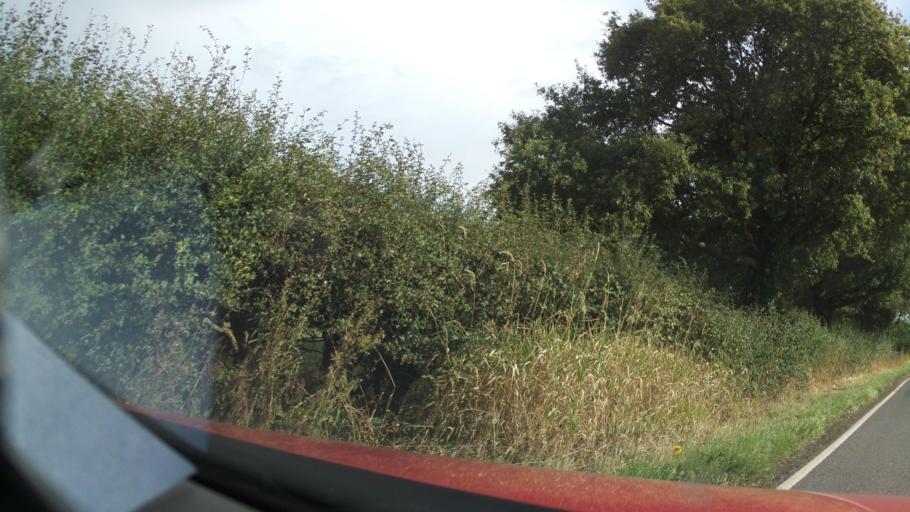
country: GB
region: England
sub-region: Telford and Wrekin
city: Madeley
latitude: 52.6338
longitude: -2.4140
